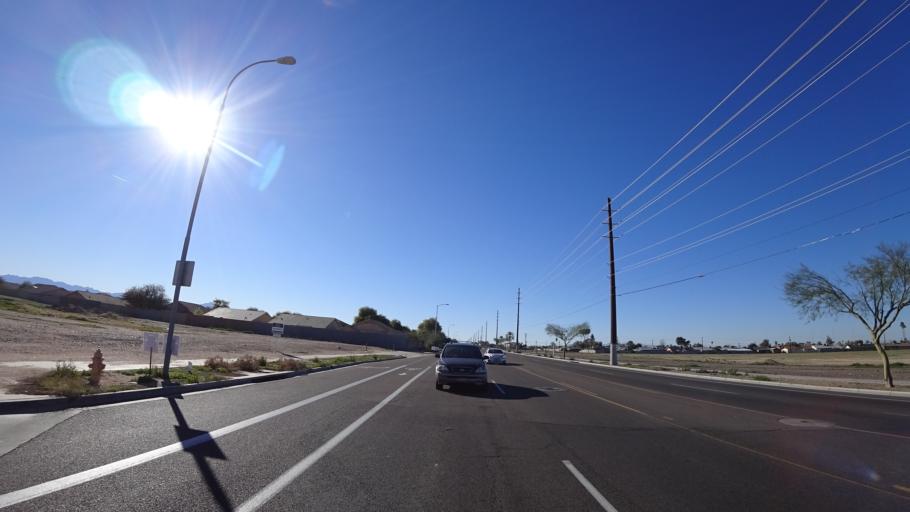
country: US
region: Arizona
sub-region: Maricopa County
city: Phoenix
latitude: 33.3922
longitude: -112.1006
